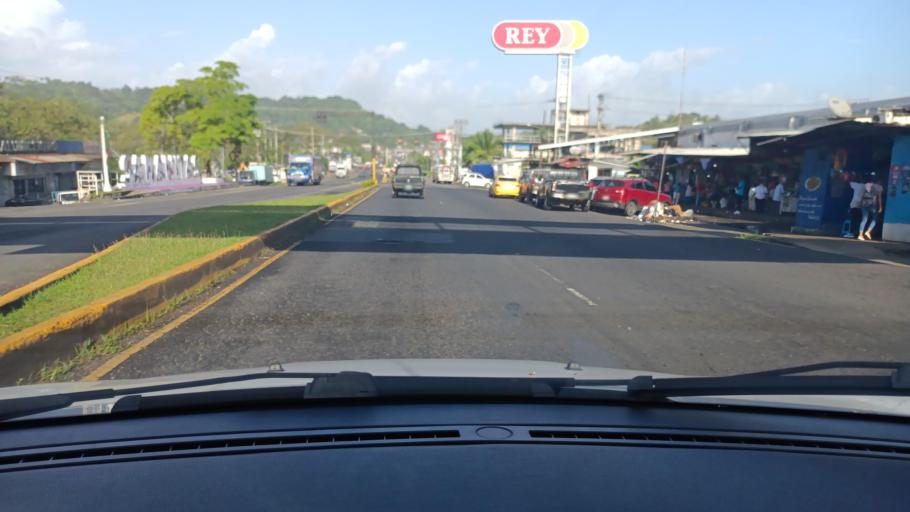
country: PA
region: Colon
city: Sabanitas
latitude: 9.3467
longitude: -79.8069
